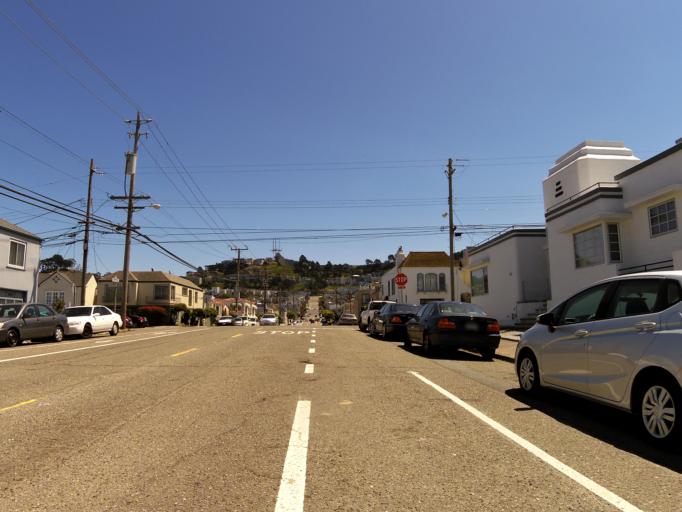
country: US
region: California
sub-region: San Mateo County
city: Daly City
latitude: 37.7522
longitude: -122.4801
